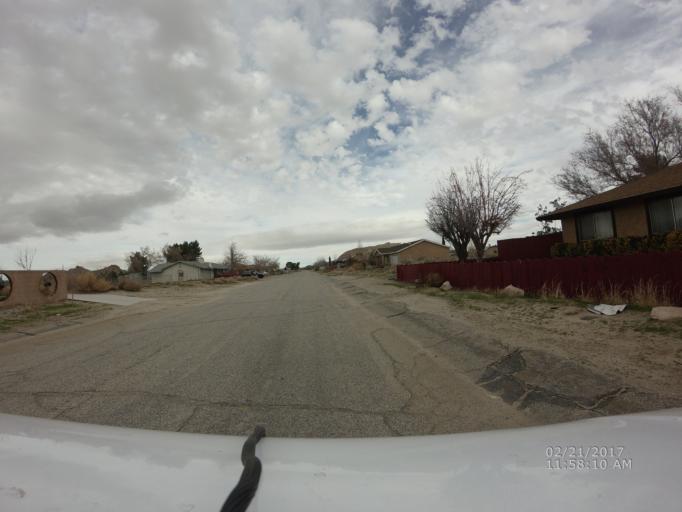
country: US
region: California
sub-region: Los Angeles County
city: Lake Los Angeles
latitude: 34.6344
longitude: -117.8583
